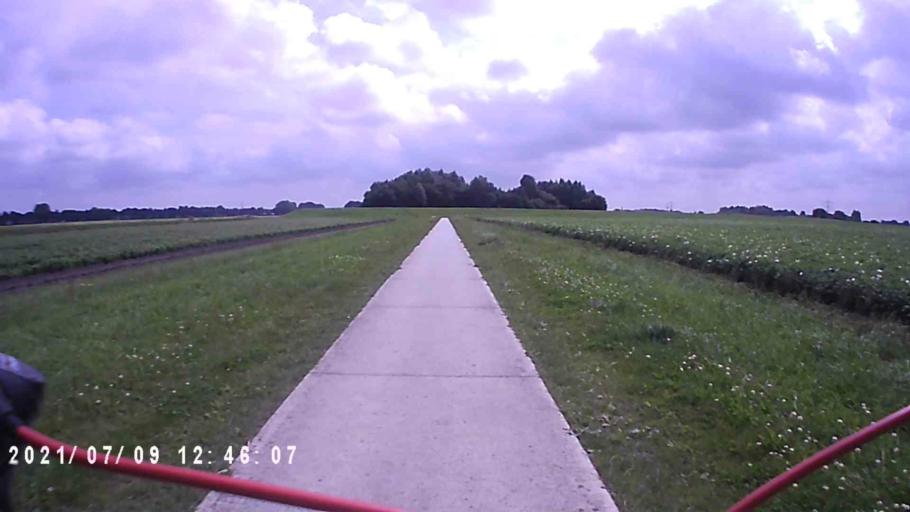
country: NL
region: Groningen
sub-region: Gemeente  Oldambt
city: Winschoten
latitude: 53.1288
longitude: 7.0265
